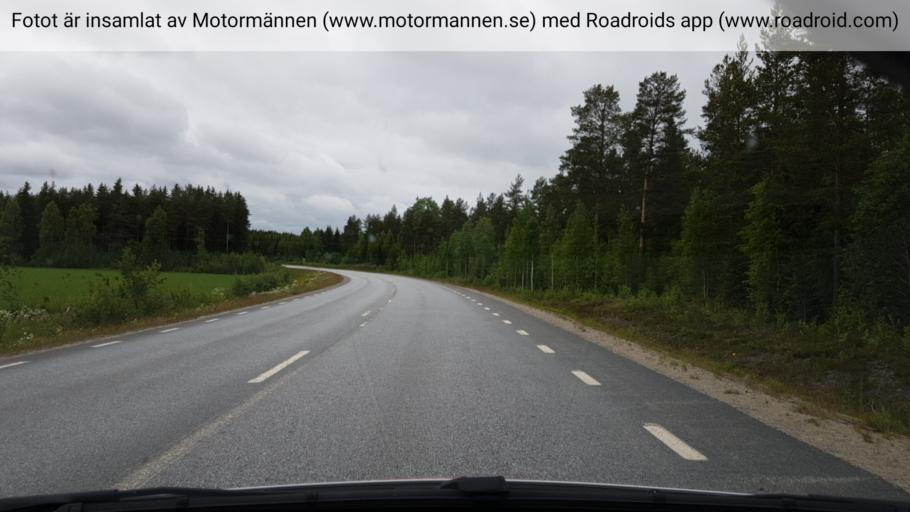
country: SE
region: Vaesterbotten
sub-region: Vannas Kommun
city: Vaennaes
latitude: 64.0043
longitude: 19.7196
